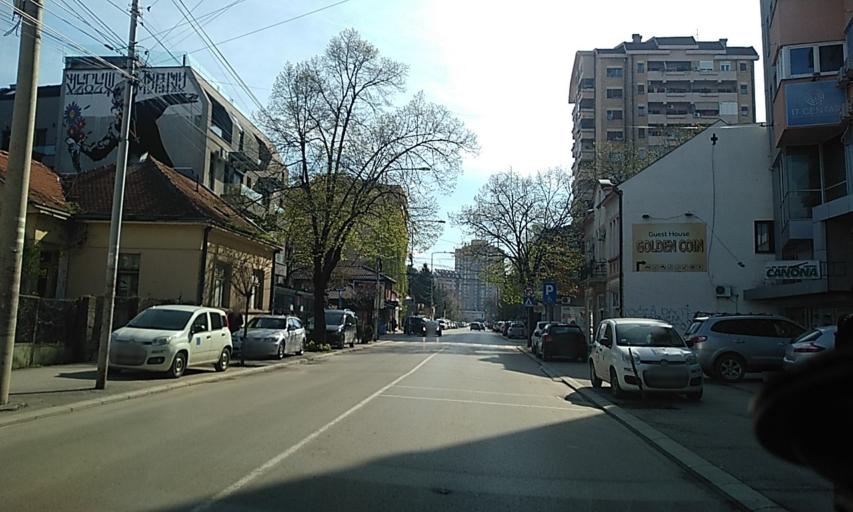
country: RS
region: Central Serbia
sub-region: Nisavski Okrug
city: Nis
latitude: 43.3179
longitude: 21.9023
